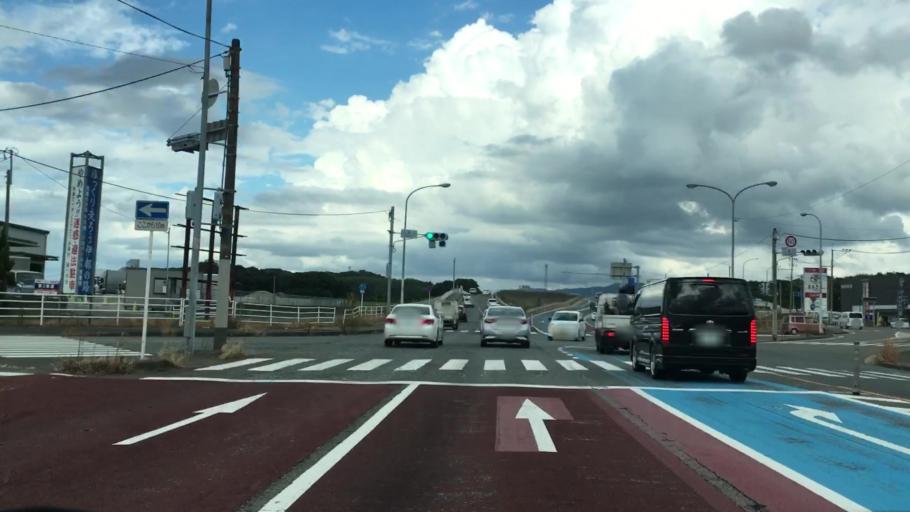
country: JP
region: Fukuoka
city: Maebaru-chuo
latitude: 33.5169
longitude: 130.1539
